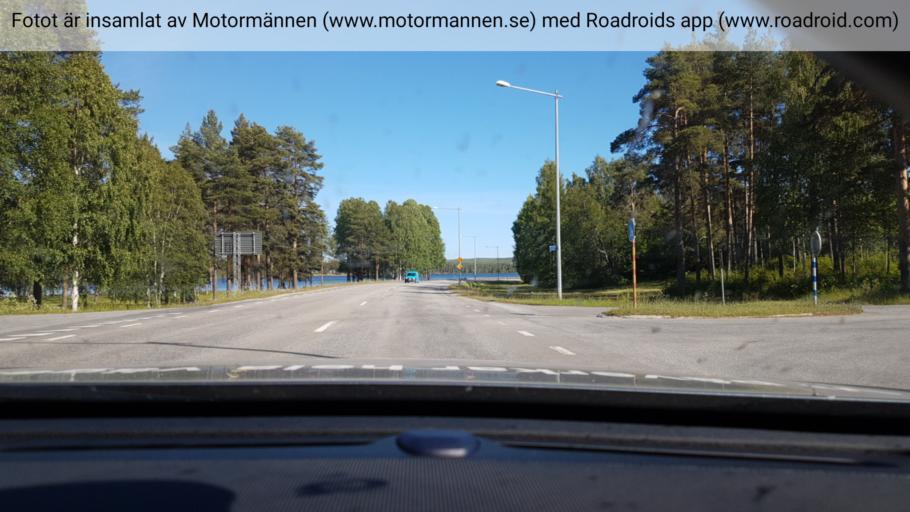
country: SE
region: Vaesterbotten
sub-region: Lycksele Kommun
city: Lycksele
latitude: 64.6036
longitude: 18.6700
